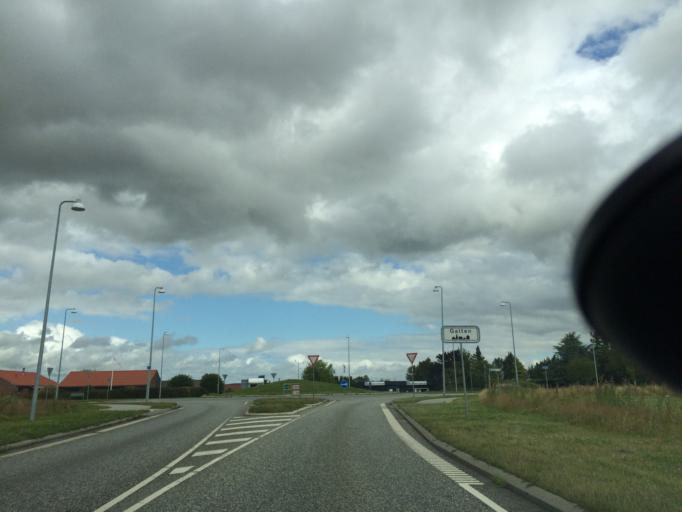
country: DK
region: Central Jutland
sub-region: Skanderborg Kommune
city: Galten
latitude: 56.1481
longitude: 9.9179
